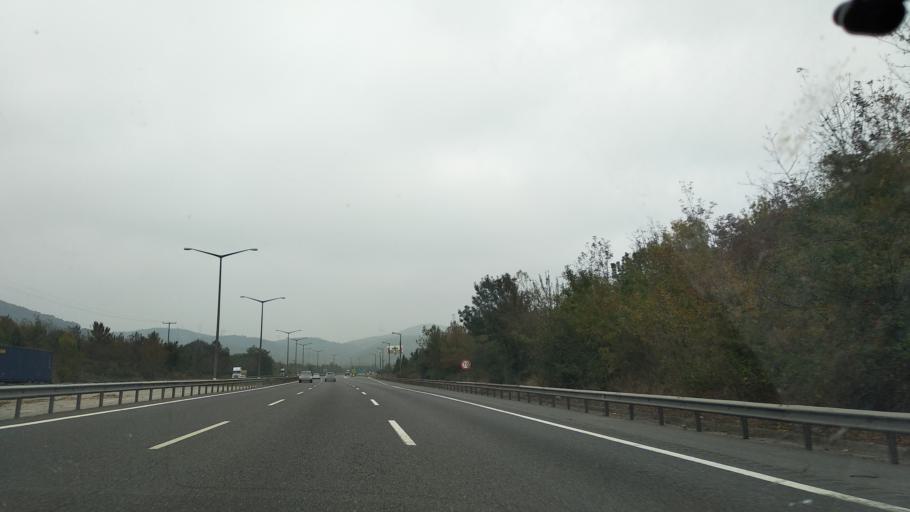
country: TR
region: Sakarya
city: Karadere
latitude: 40.7980
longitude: 30.8461
